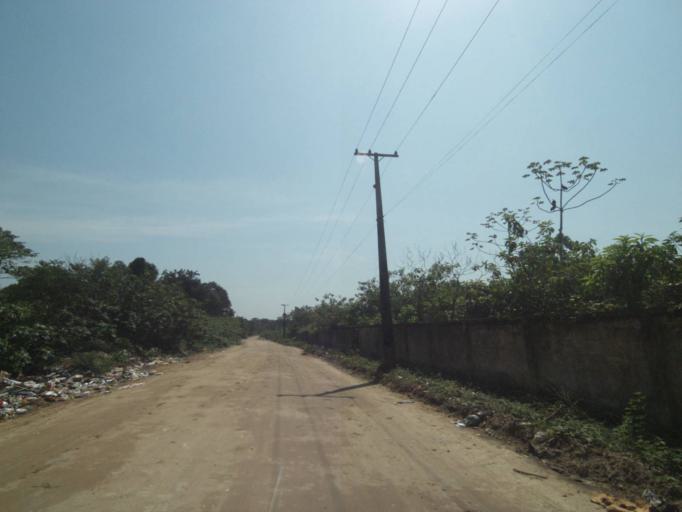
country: BR
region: Parana
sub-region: Paranagua
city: Paranagua
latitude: -25.5448
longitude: -48.5700
